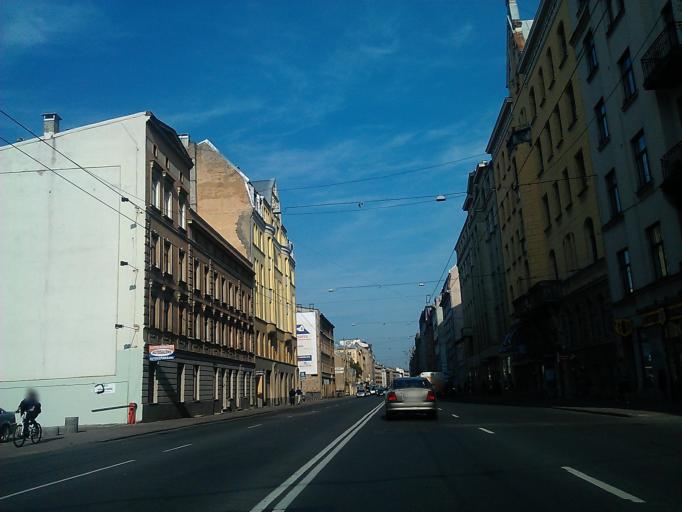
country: LV
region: Riga
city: Riga
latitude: 56.9634
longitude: 24.1380
